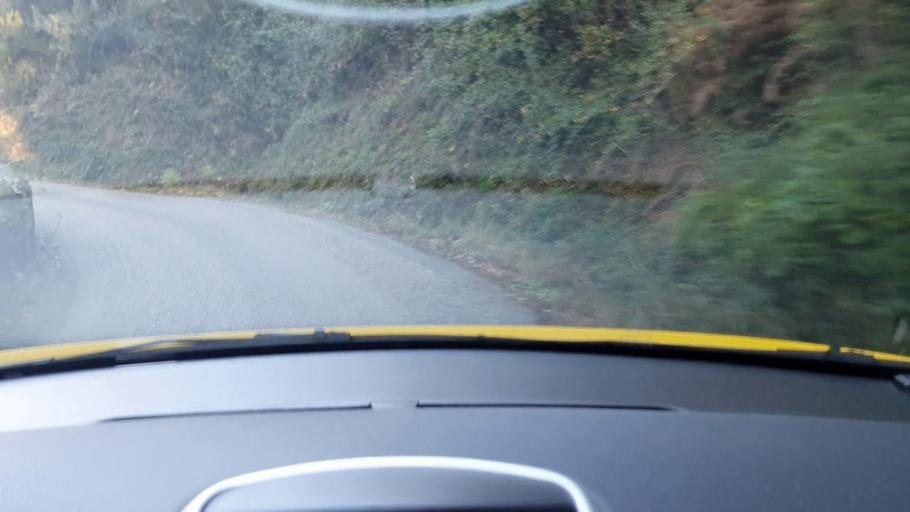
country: FR
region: Languedoc-Roussillon
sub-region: Departement du Gard
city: Branoux-les-Taillades
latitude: 44.2568
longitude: 3.9774
